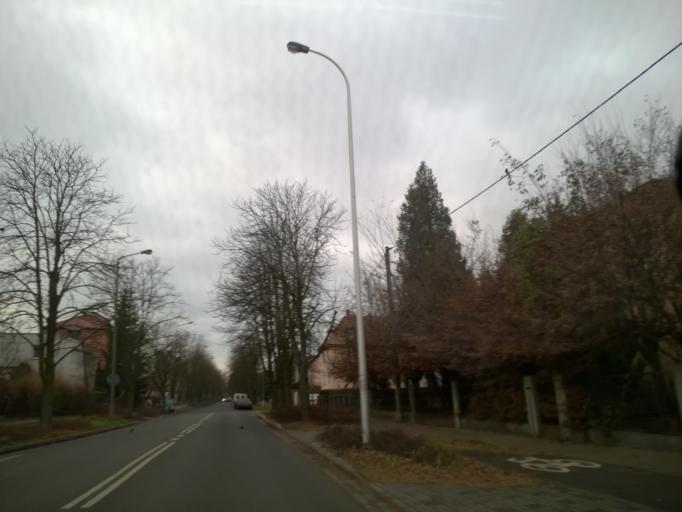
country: PL
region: Lower Silesian Voivodeship
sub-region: Powiat wroclawski
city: Wroclaw
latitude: 51.0707
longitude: 17.0100
